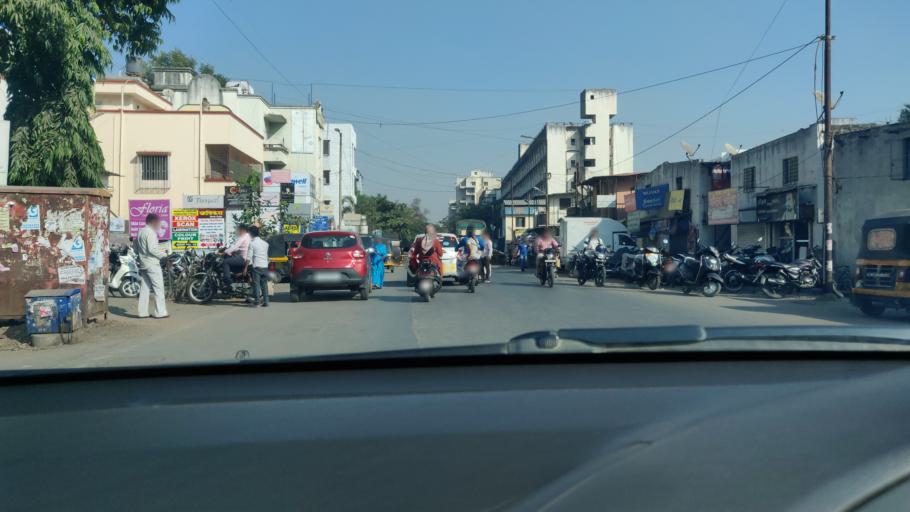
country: IN
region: Maharashtra
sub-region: Pune Division
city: Khadki
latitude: 18.5609
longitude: 73.8030
